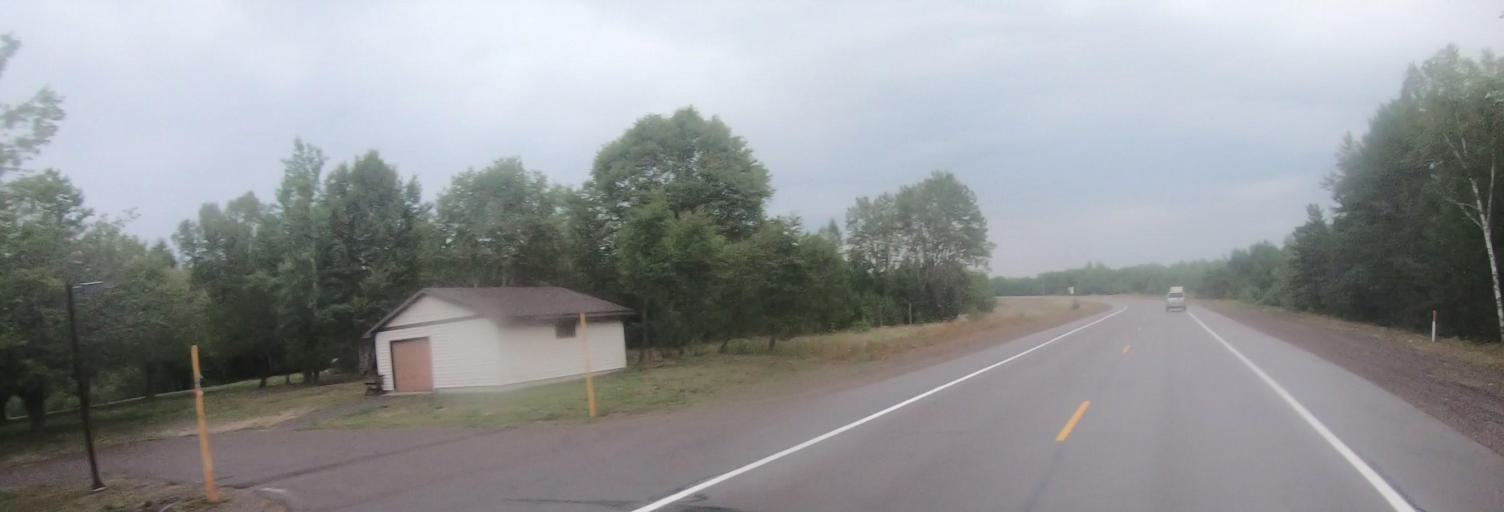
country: US
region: Michigan
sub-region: Houghton County
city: Laurium
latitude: 47.3003
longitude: -88.3800
